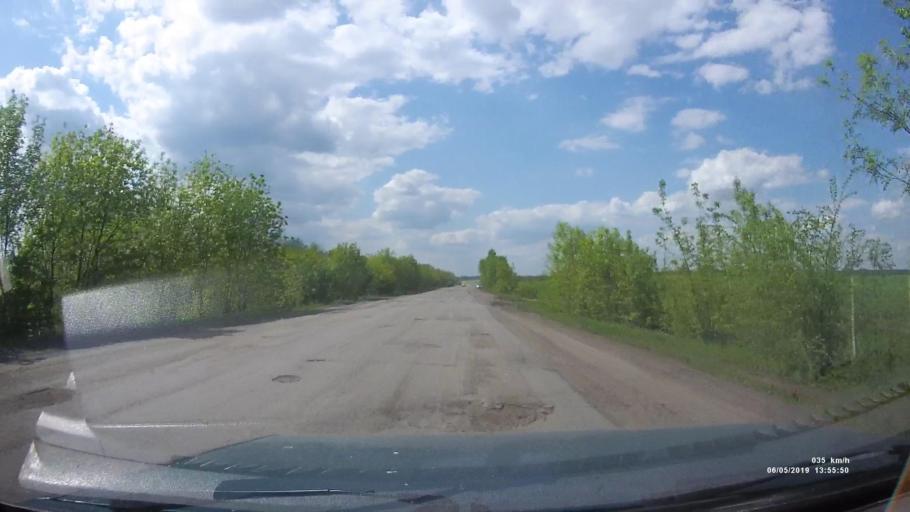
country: RU
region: Rostov
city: Melikhovskaya
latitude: 47.6792
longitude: 40.4357
